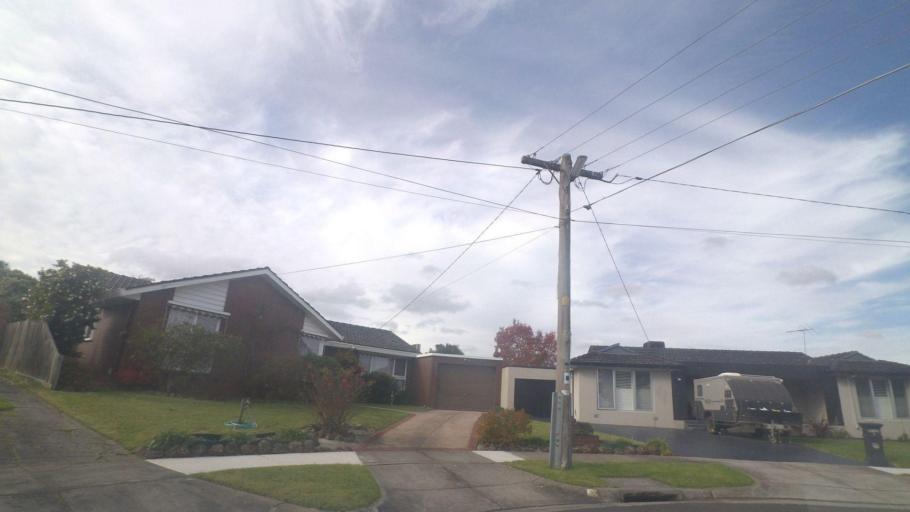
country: AU
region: Victoria
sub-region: Whitehorse
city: Vermont South
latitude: -37.8639
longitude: 145.1784
